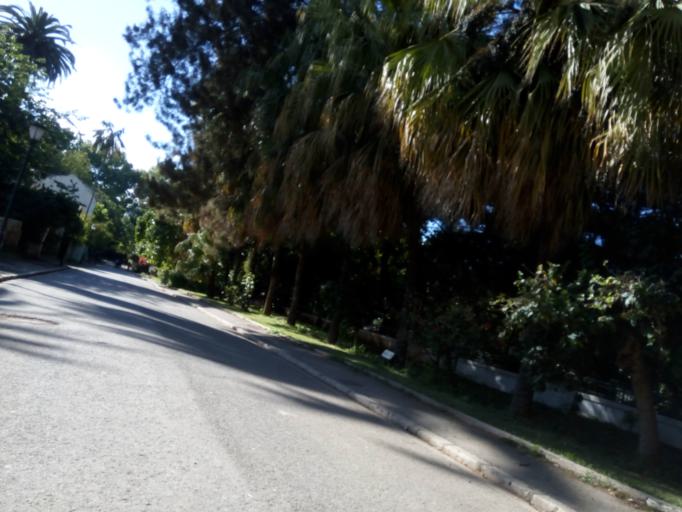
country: DZ
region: Alger
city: Algiers
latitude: 36.7460
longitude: 3.0751
